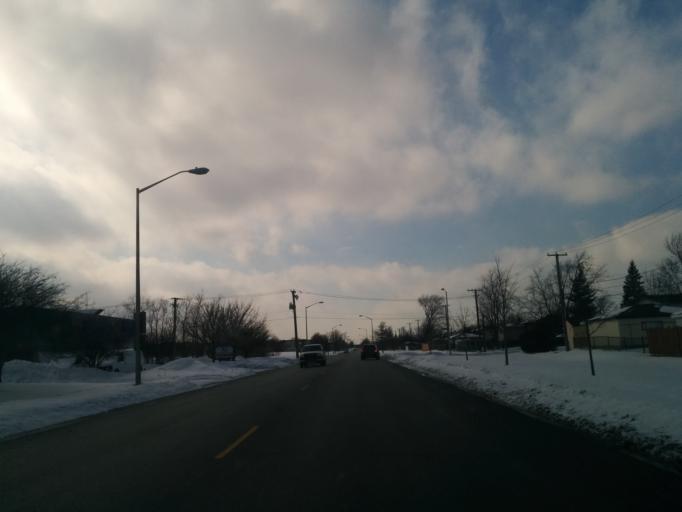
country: US
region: Illinois
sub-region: Cook County
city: Tinley Park
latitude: 41.5730
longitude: -87.8019
